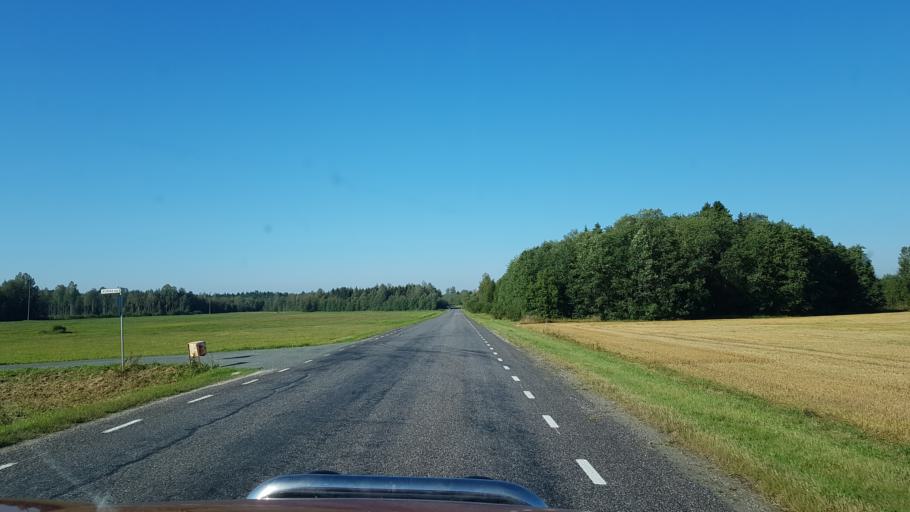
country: EE
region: Jogevamaa
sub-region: Jogeva linn
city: Jogeva
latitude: 58.6968
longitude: 26.3808
